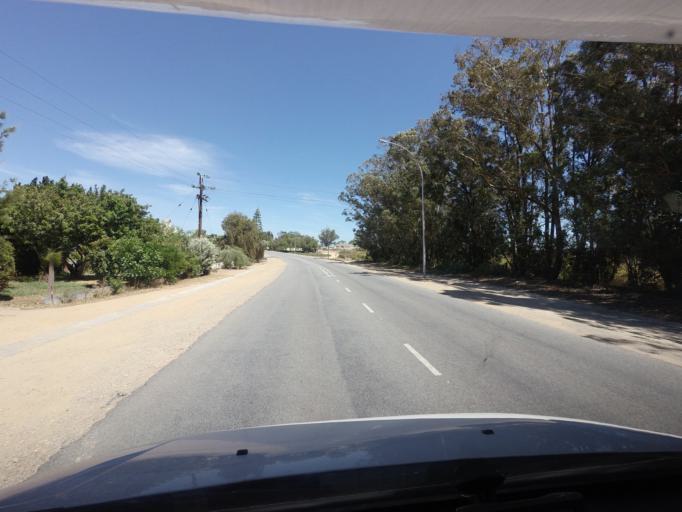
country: ZA
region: Western Cape
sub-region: West Coast District Municipality
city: Vredenburg
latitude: -32.7855
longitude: 18.1907
